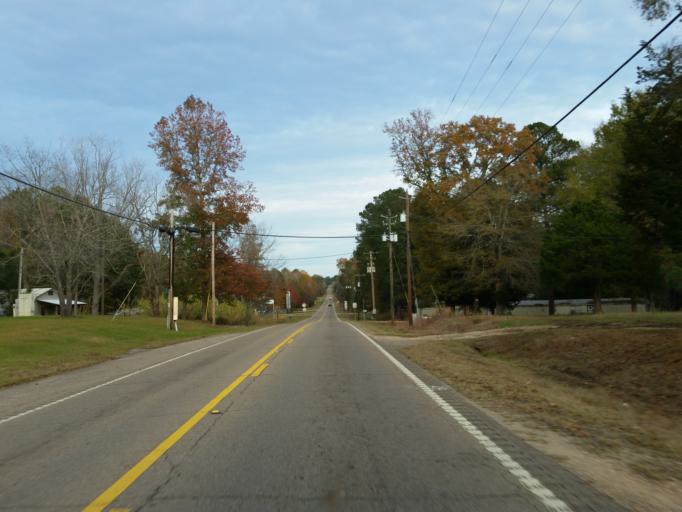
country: US
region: Mississippi
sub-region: Lauderdale County
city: Marion
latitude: 32.4039
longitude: -88.5935
